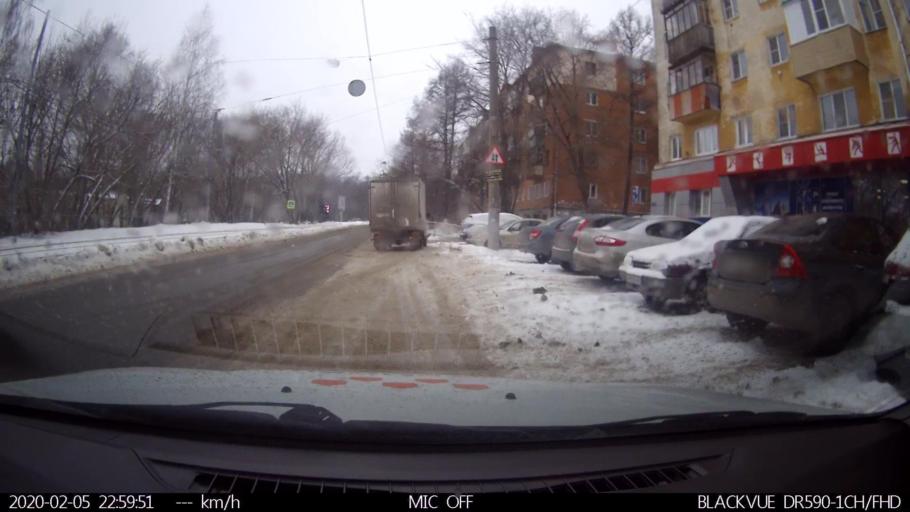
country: RU
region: Penza
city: Bogoslovka
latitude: 53.1848
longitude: 44.8725
